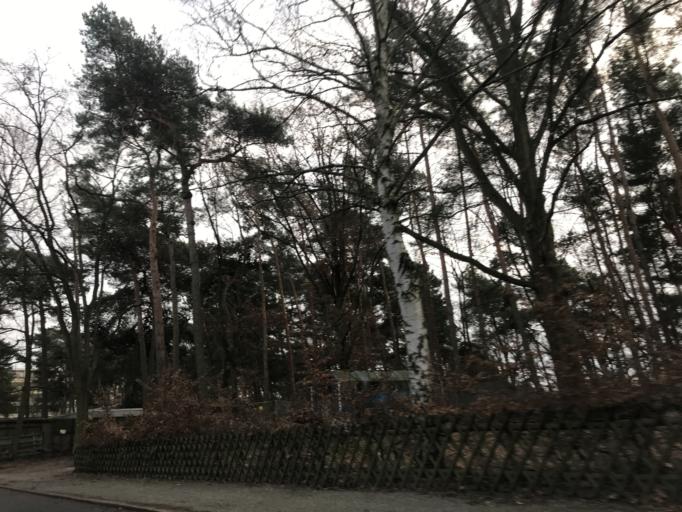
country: DE
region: Berlin
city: Falkenhagener Feld
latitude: 52.5609
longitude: 13.1524
